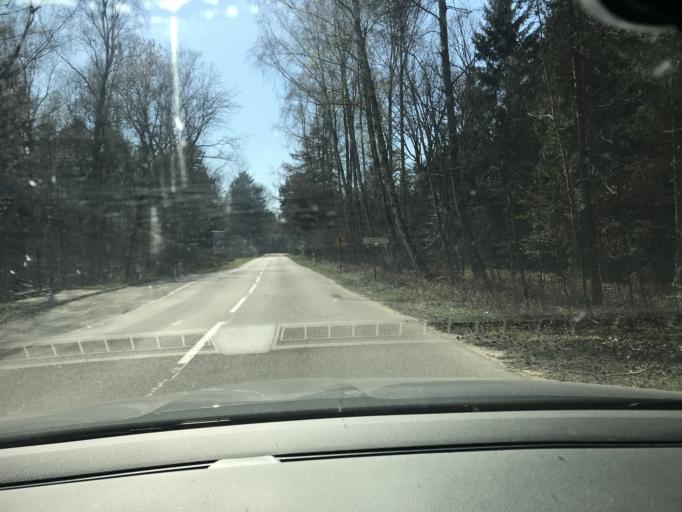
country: PL
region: Pomeranian Voivodeship
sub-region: Powiat nowodworski
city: Krynica Morska
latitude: 54.3592
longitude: 19.3420
